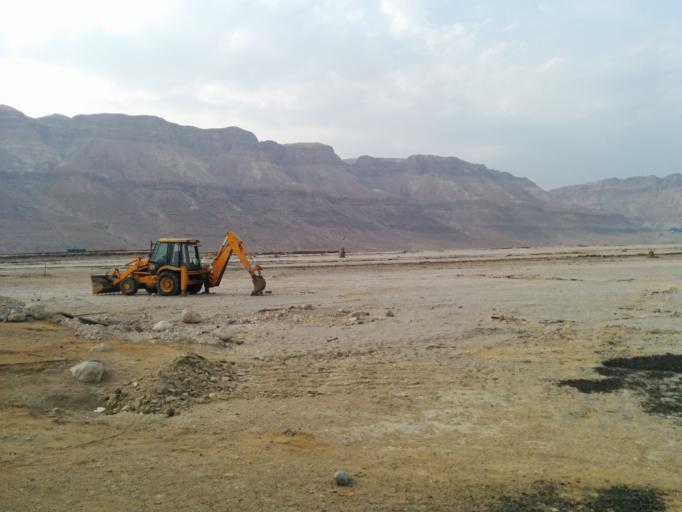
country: PS
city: `Arab ar Rashaydah
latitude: 31.4208
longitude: 35.3908
